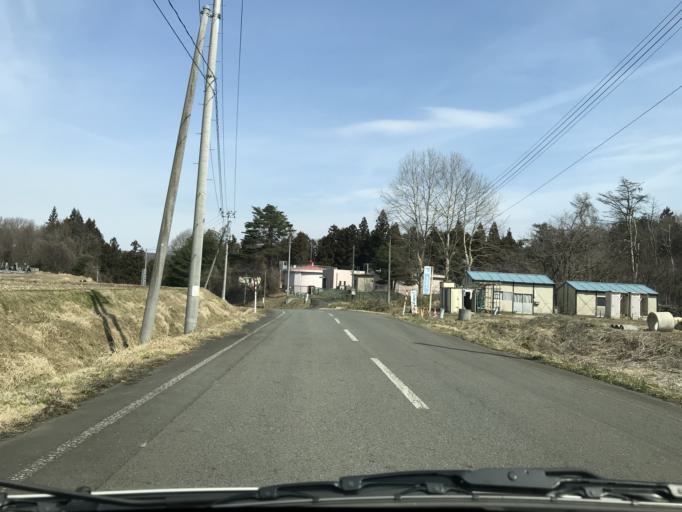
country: JP
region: Iwate
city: Mizusawa
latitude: 39.1166
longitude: 141.0127
